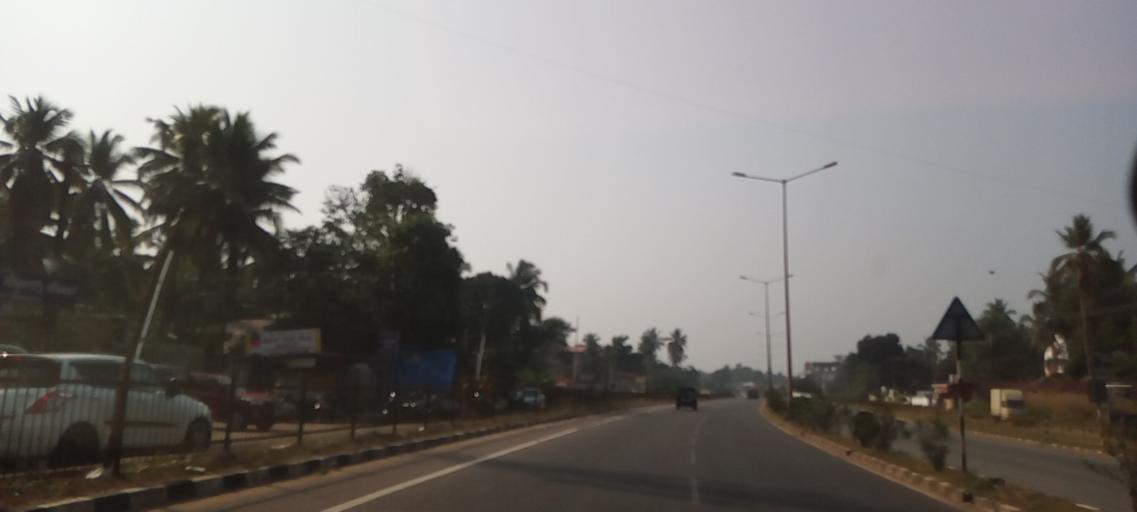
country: IN
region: Karnataka
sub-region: Udupi
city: Coondapoor
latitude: 13.5244
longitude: 74.7059
